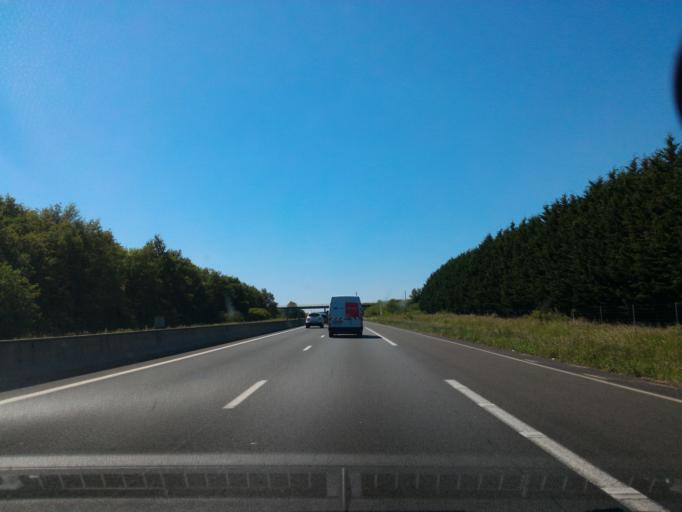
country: FR
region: Centre
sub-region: Departement d'Indre-et-Loire
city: Sorigny
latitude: 47.2332
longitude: 0.6589
